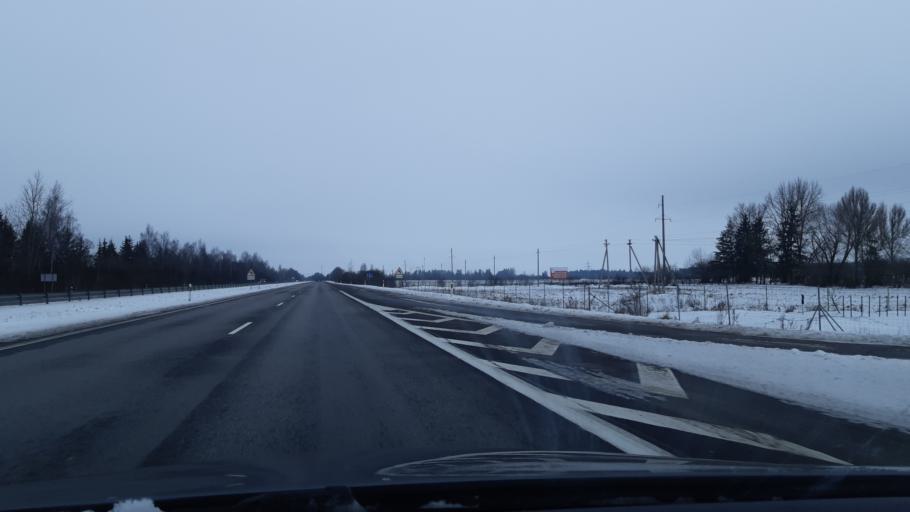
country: LT
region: Kauno apskritis
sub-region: Kaunas
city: Sargenai
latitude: 55.0731
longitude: 23.8147
